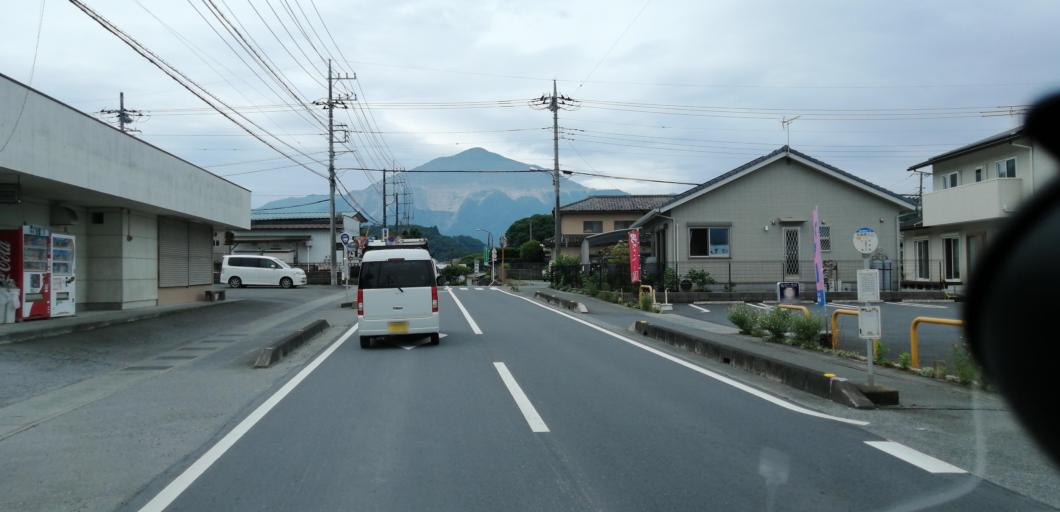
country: JP
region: Saitama
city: Chichibu
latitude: 36.0154
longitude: 139.1124
